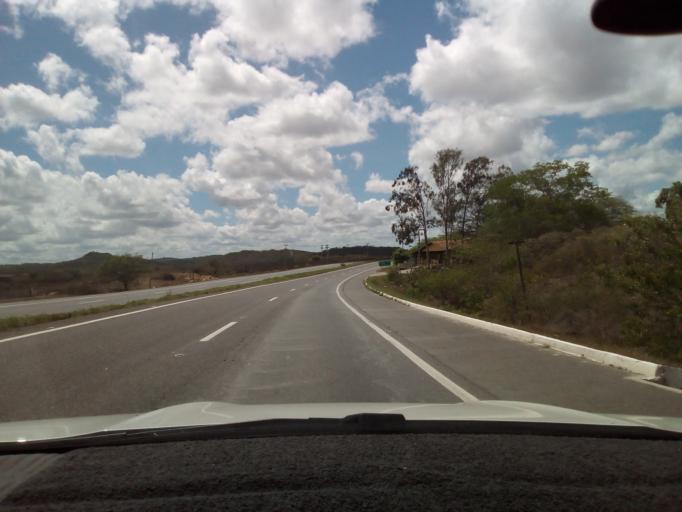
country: BR
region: Paraiba
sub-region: Massaranduba
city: Massaranduba
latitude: -7.2575
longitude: -35.8131
